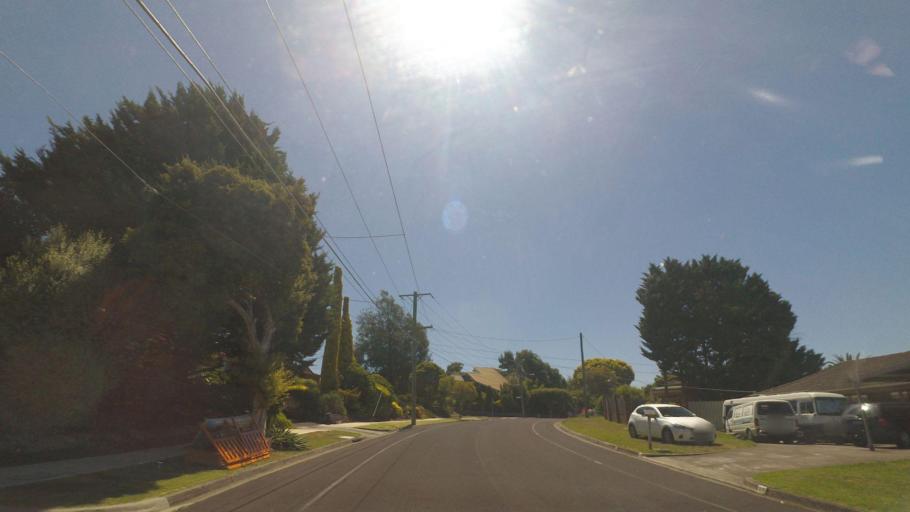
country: AU
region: Victoria
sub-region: Yarra Ranges
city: Chirnside Park
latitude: -37.7567
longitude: 145.3224
